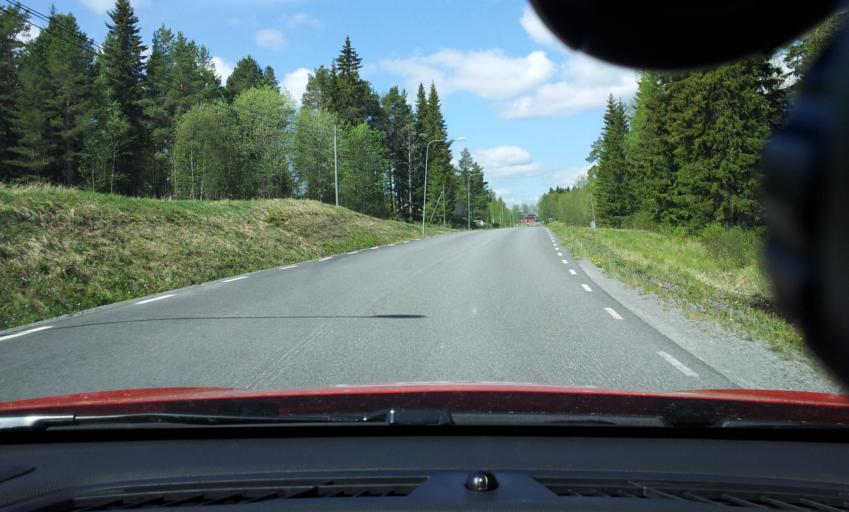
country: SE
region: Jaemtland
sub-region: OEstersunds Kommun
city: Ostersund
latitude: 62.9920
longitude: 14.5887
